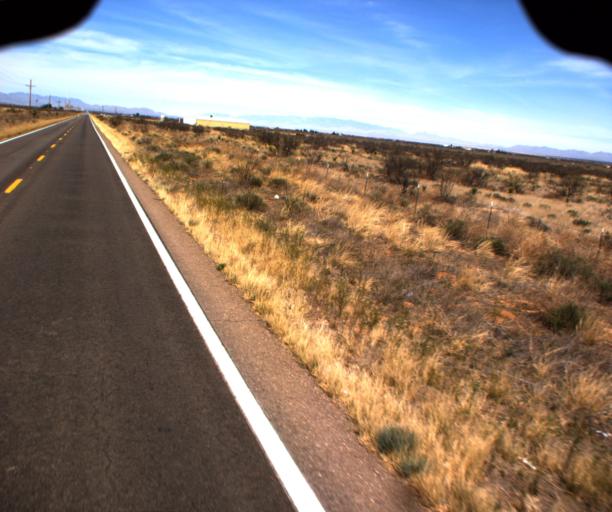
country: US
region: Arizona
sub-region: Cochise County
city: Willcox
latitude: 31.9927
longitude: -109.8572
